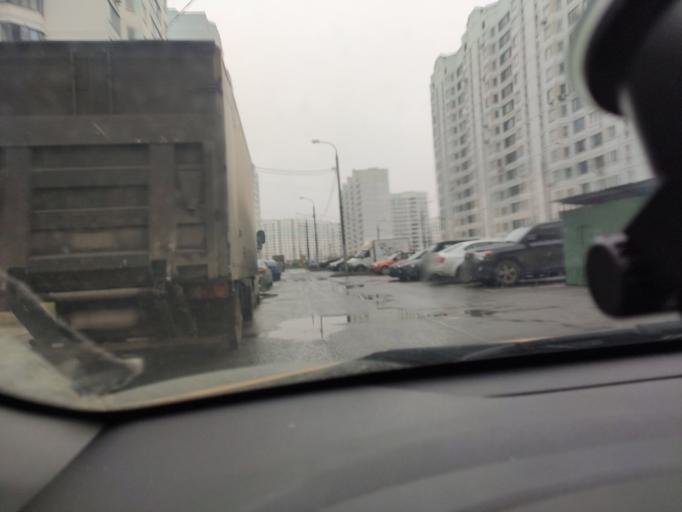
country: RU
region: Moskovskaya
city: Shcherbinka
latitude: 55.5038
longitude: 37.5881
